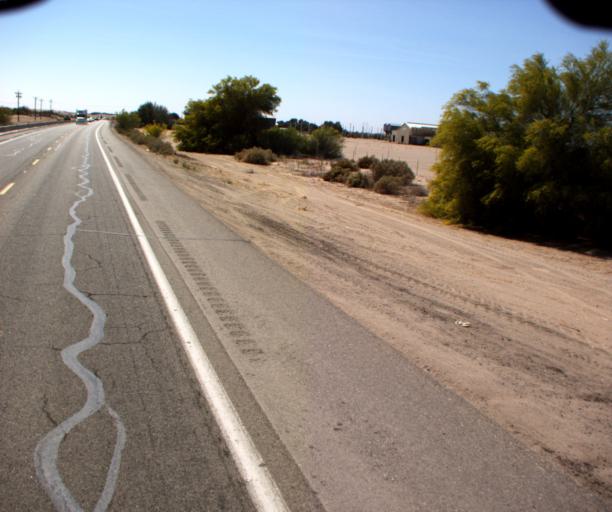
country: US
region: Arizona
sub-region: Yuma County
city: Fortuna Foothills
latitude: 32.7098
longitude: -114.4304
